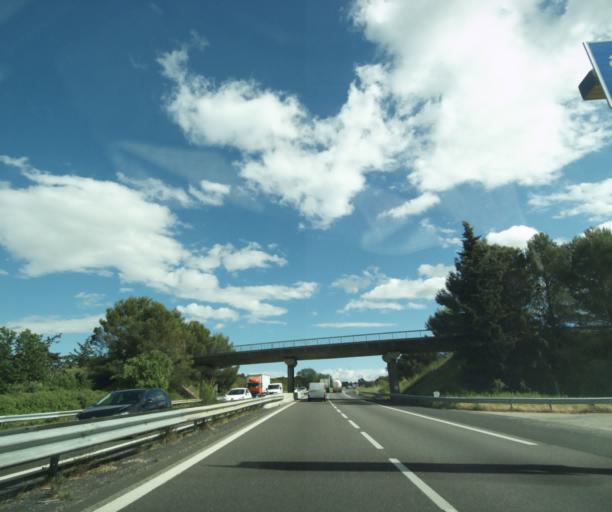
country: FR
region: Languedoc-Roussillon
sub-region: Departement du Gard
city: Caissargues
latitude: 43.7923
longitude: 4.3968
